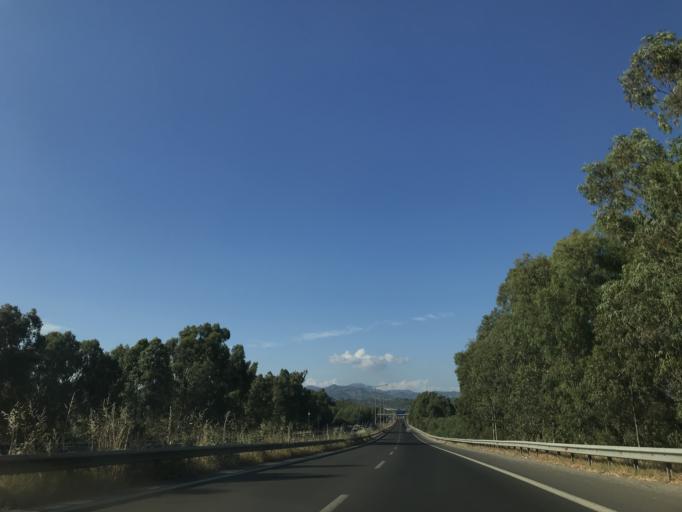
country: TR
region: Aydin
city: Germencik
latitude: 37.8638
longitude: 27.5656
